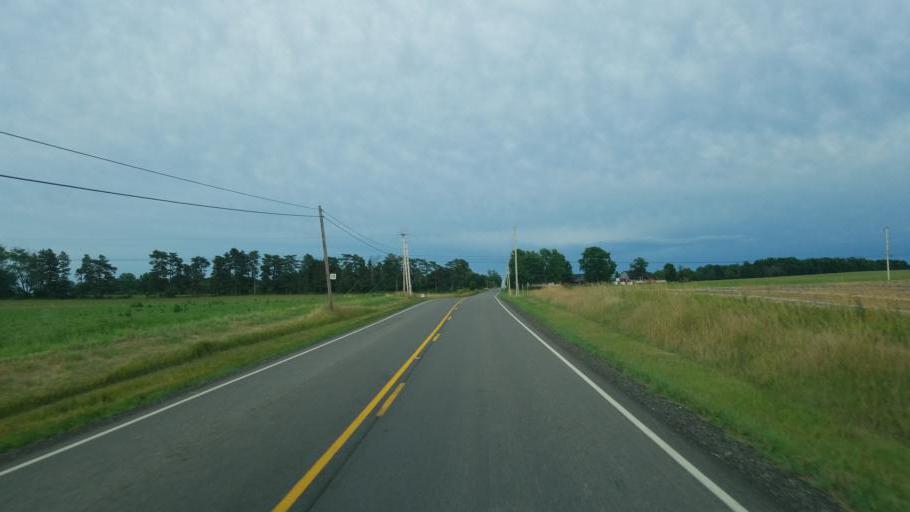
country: US
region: Ohio
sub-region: Richland County
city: Lincoln Heights
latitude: 40.9035
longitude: -82.4756
